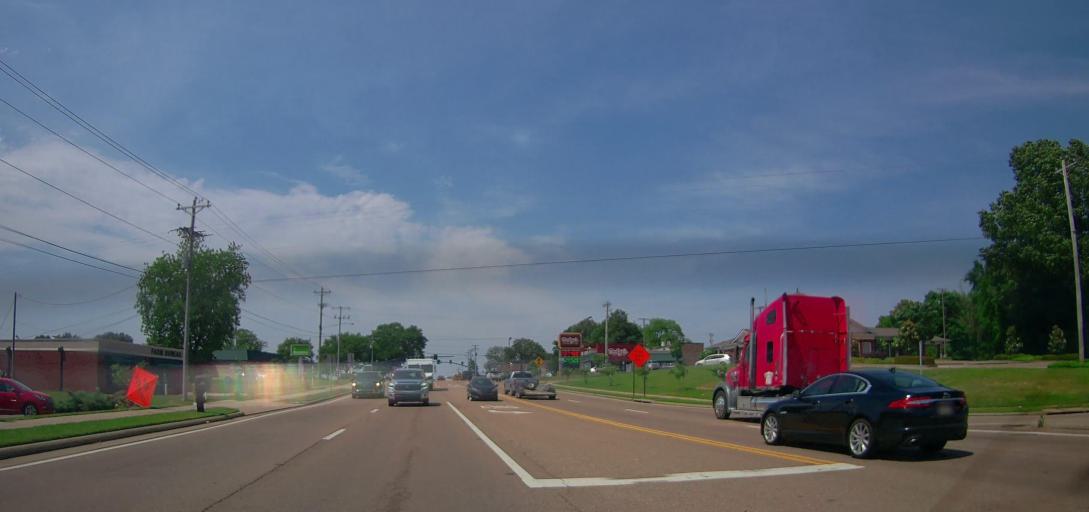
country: US
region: Mississippi
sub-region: De Soto County
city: Olive Branch
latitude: 34.9603
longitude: -89.8304
